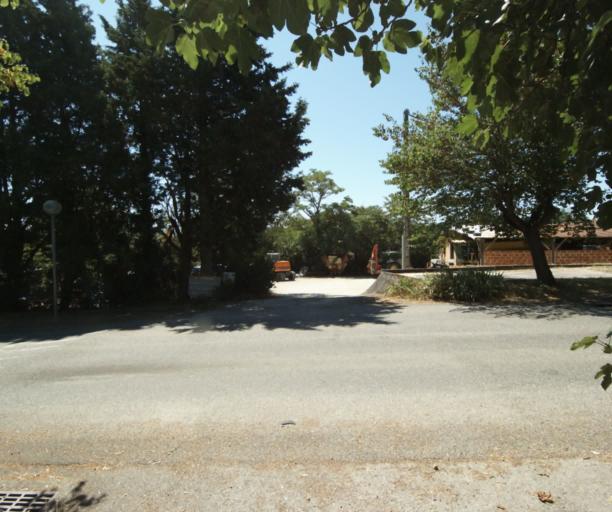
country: FR
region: Midi-Pyrenees
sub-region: Departement de la Haute-Garonne
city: Saint-Felix-Lauragais
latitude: 43.4779
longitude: 1.9253
